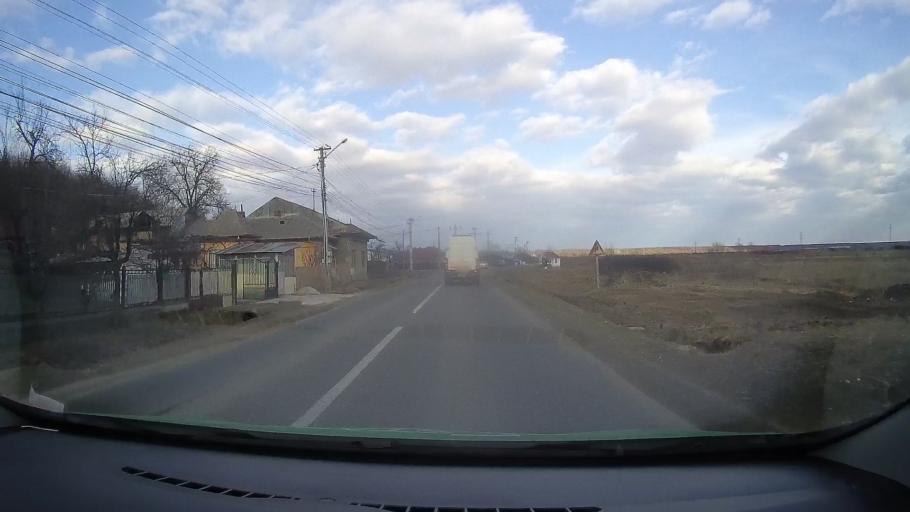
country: RO
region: Dambovita
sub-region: Comuna Gura Ocnitei
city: Gura Ocnitei
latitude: 44.9316
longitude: 25.5598
